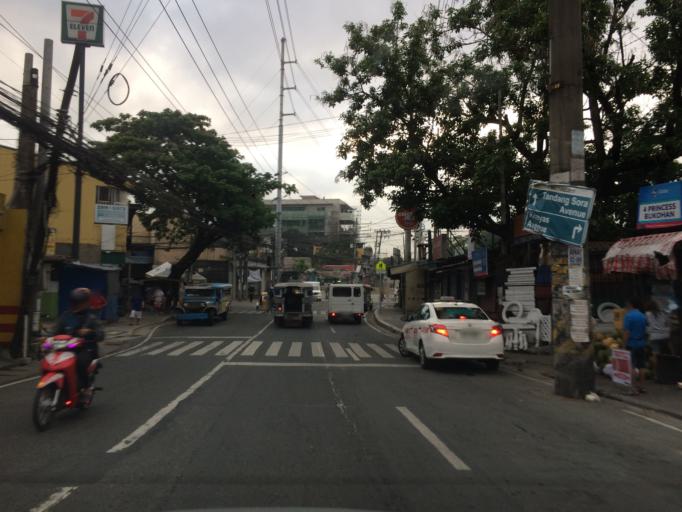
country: PH
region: Calabarzon
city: Bagong Pagasa
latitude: 14.6737
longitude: 121.0484
